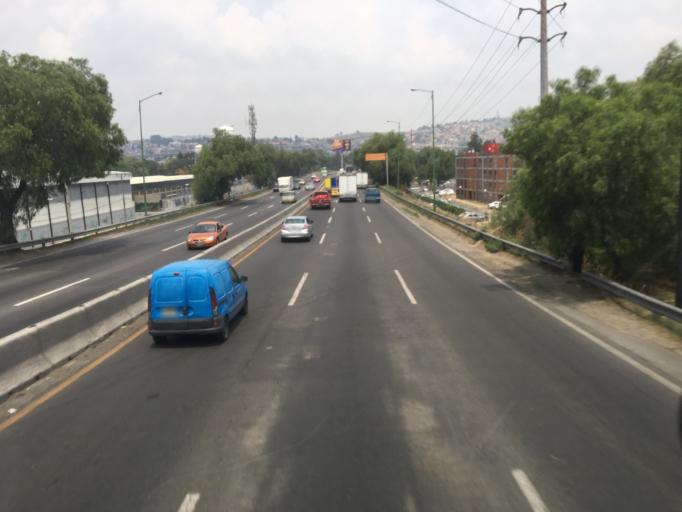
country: MX
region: Mexico
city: Tlalnepantla
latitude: 19.5604
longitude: -99.1955
